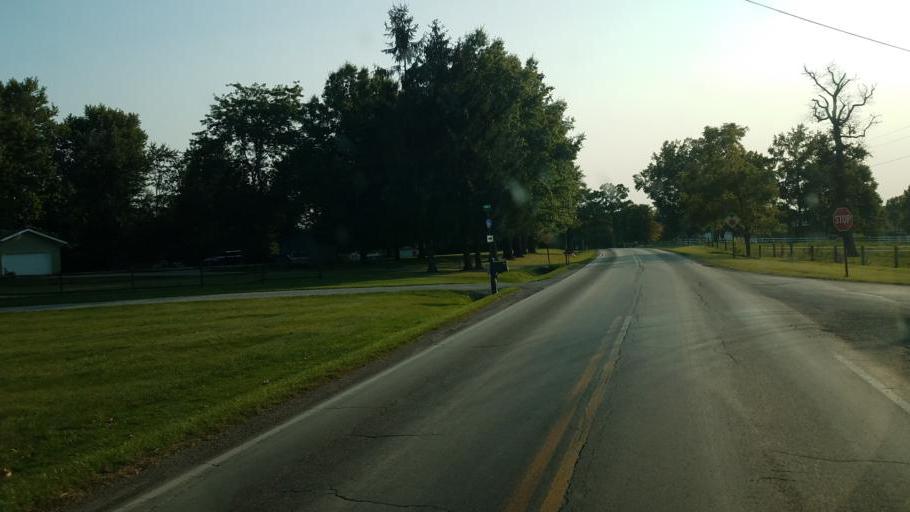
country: US
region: Ohio
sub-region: Wayne County
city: Apple Creek
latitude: 40.7430
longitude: -81.8140
